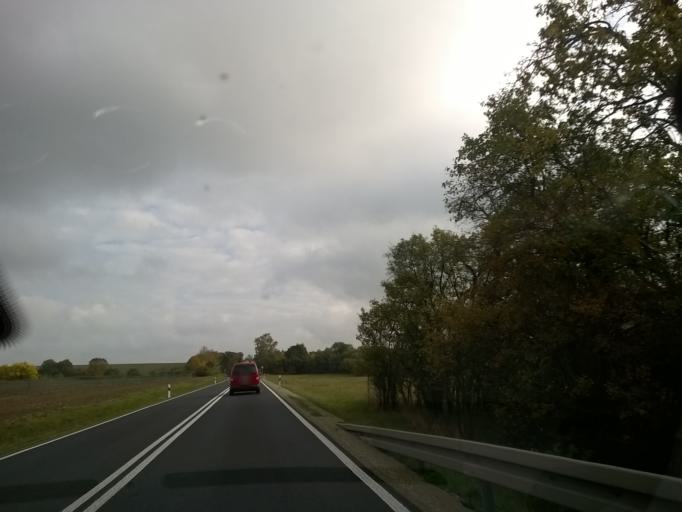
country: DE
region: Thuringia
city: Wasserthaleben
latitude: 51.2969
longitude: 10.8873
